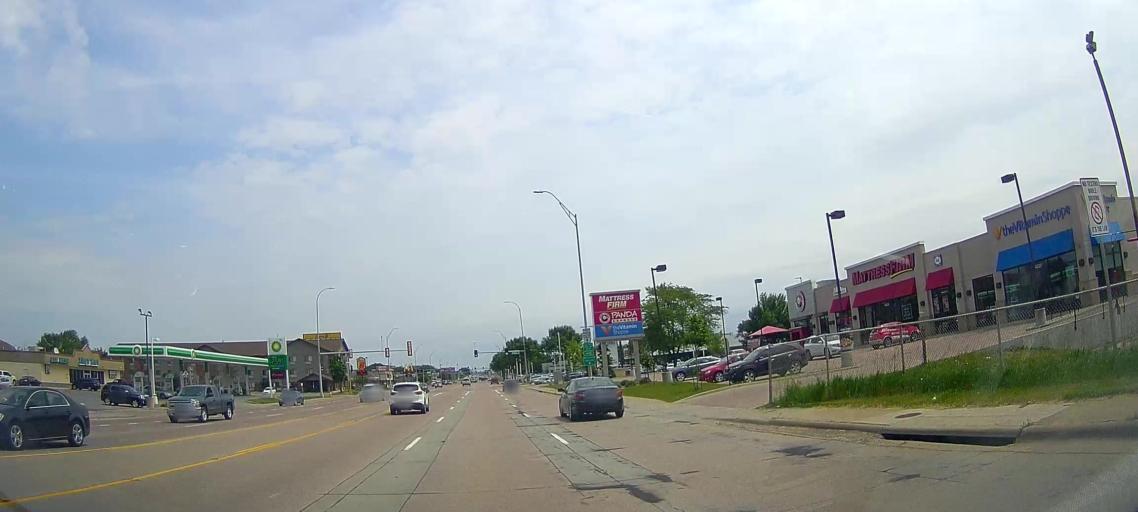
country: US
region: South Dakota
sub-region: Minnehaha County
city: Sioux Falls
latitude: 43.5148
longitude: -96.7780
